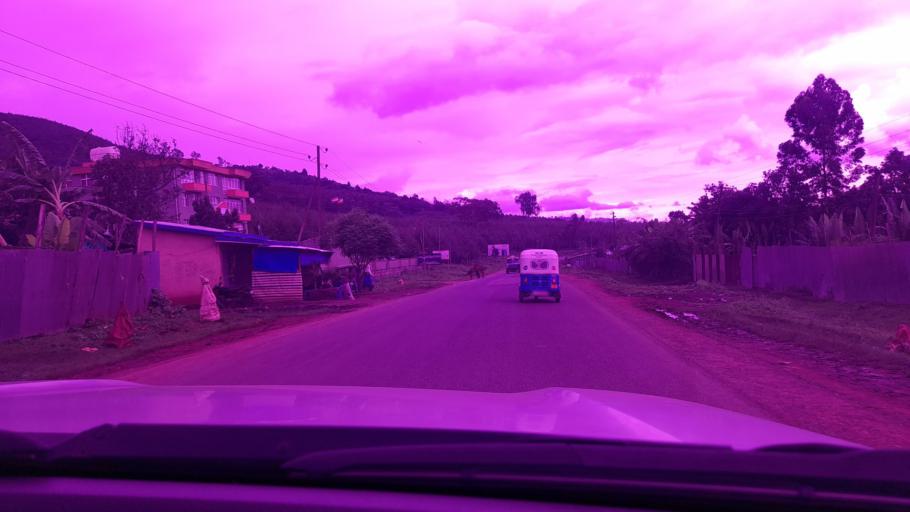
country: ET
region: Oromiya
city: Jima
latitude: 7.6689
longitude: 36.8703
